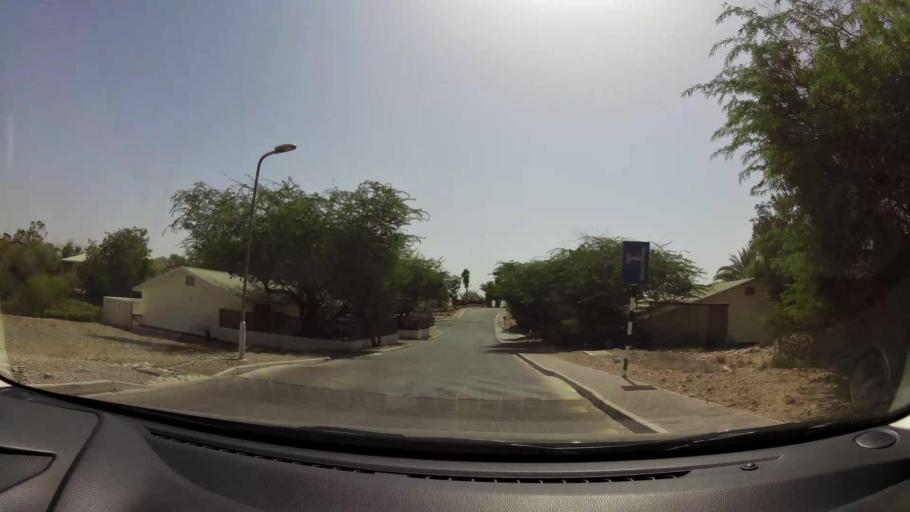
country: OM
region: Muhafazat Masqat
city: Muscat
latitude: 23.6296
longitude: 58.4962
